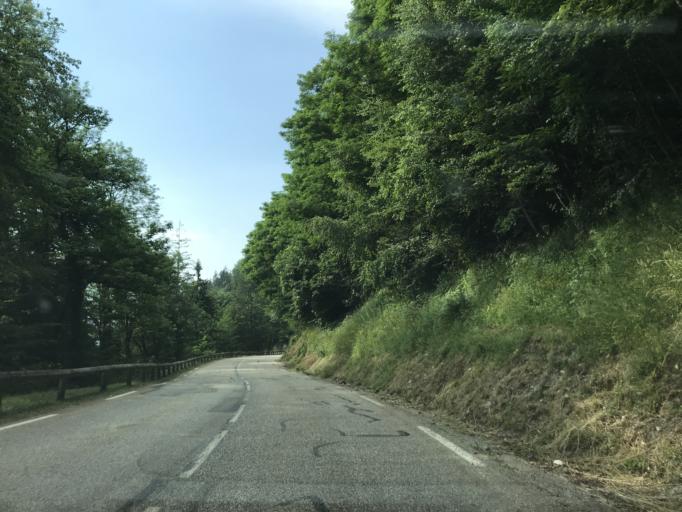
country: FR
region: Rhone-Alpes
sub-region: Departement de l'Isere
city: Allevard
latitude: 45.3735
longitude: 6.0961
